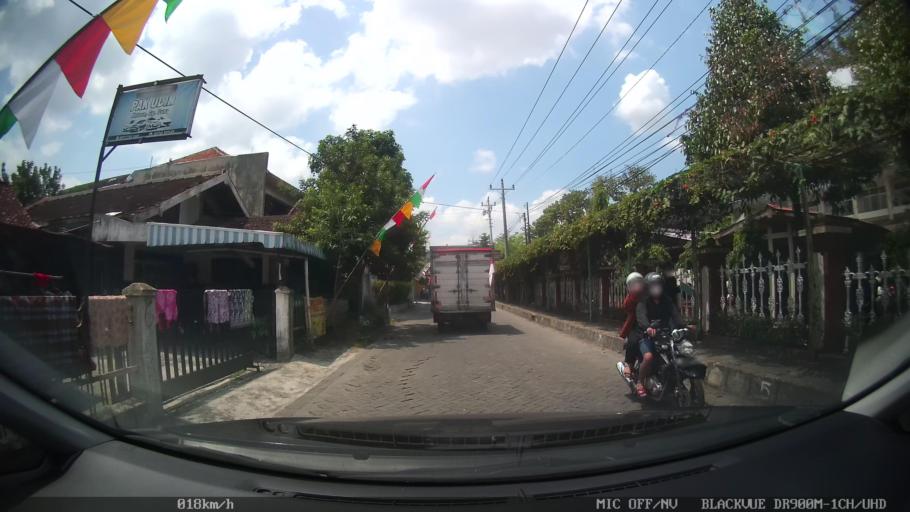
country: ID
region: Daerah Istimewa Yogyakarta
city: Yogyakarta
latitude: -7.7731
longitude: 110.3875
